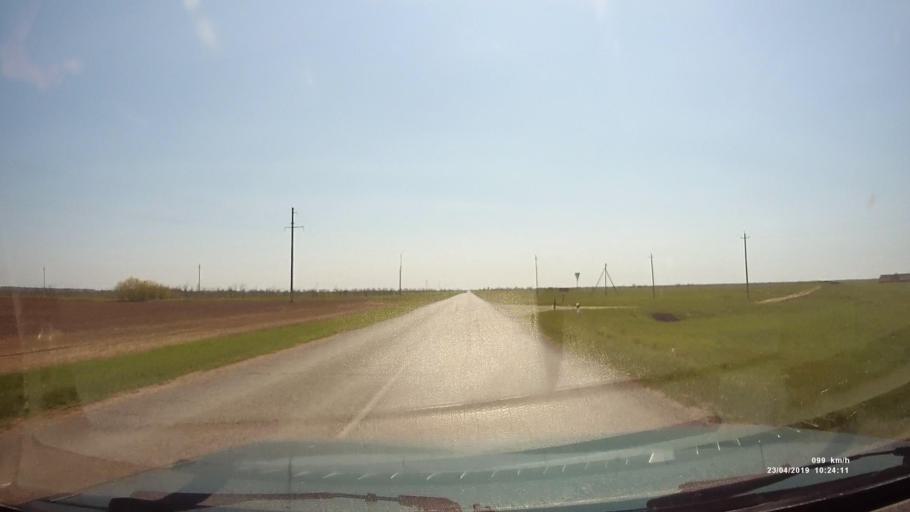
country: RU
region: Rostov
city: Sovetskoye
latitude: 46.6410
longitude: 42.4373
